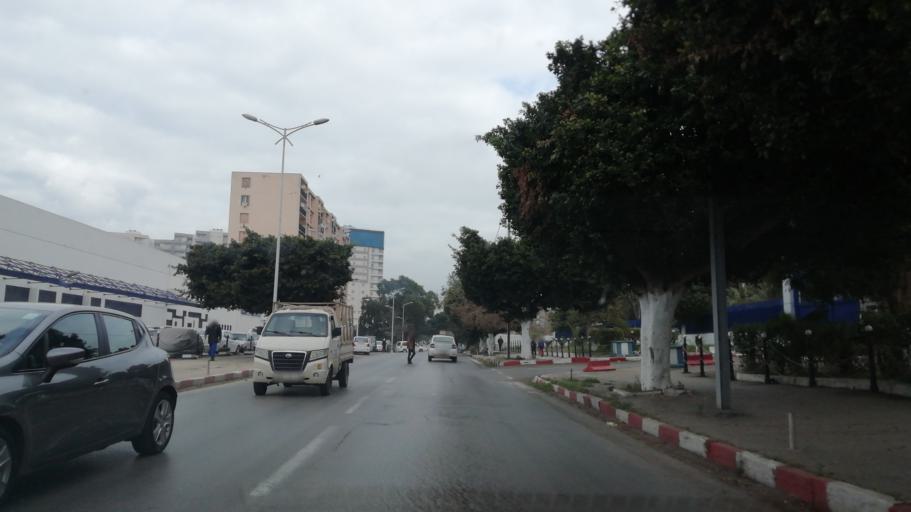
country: DZ
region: Oran
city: Oran
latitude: 35.6997
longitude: -0.6121
